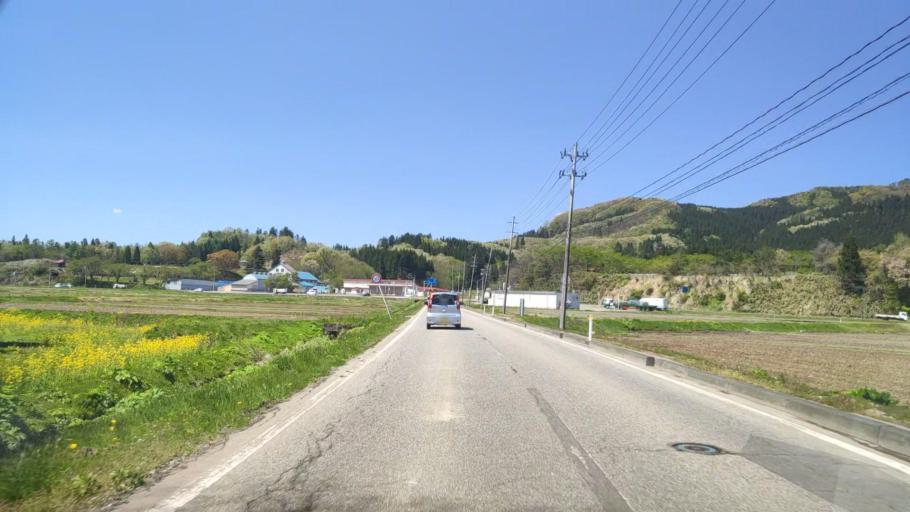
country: JP
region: Akita
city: Omagari
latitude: 39.4472
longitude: 140.4513
